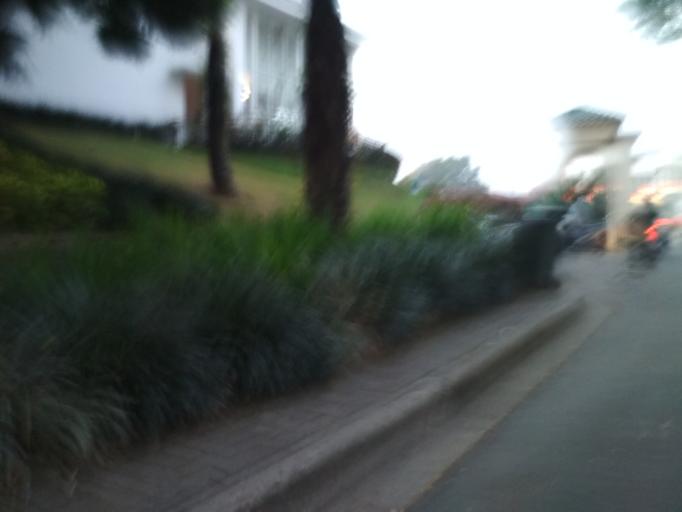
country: ID
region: West Java
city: Caringin
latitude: -6.6626
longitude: 106.8444
